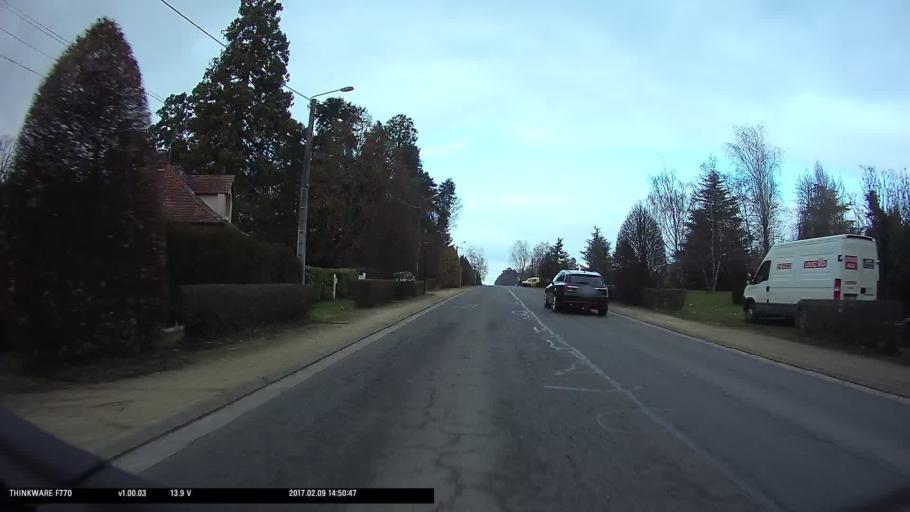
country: FR
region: Centre
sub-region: Departement du Cher
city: Levet
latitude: 46.9303
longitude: 2.4028
